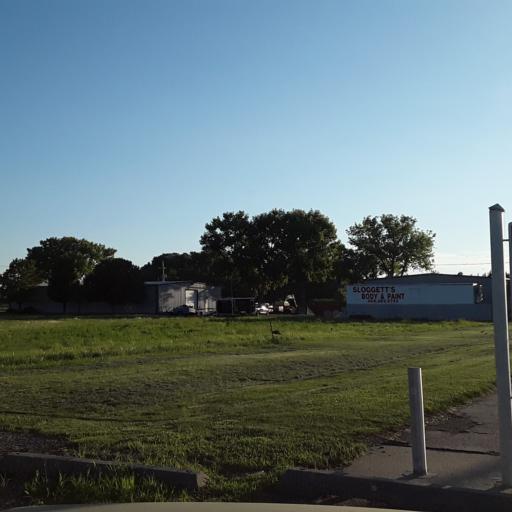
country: US
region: Nebraska
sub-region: Hall County
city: Grand Island
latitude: 40.9310
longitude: -98.3234
